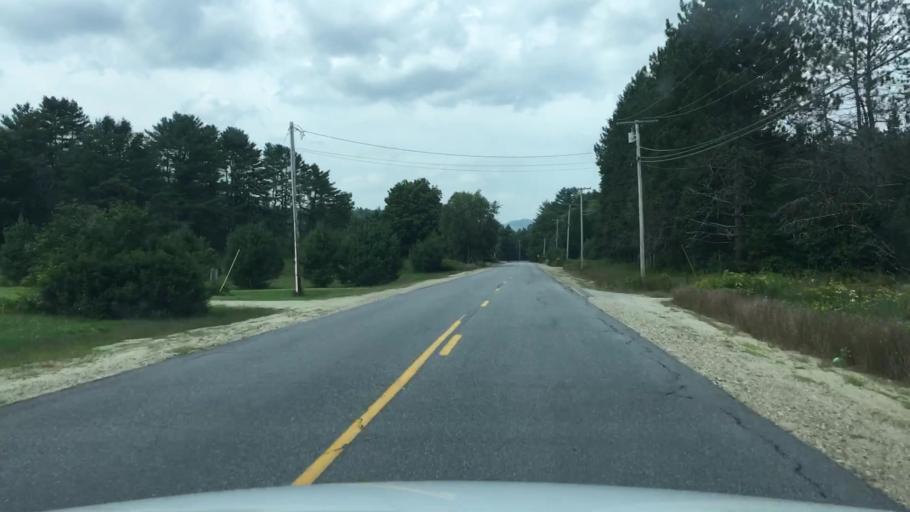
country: US
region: Maine
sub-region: Oxford County
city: Rumford
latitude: 44.5144
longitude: -70.6210
